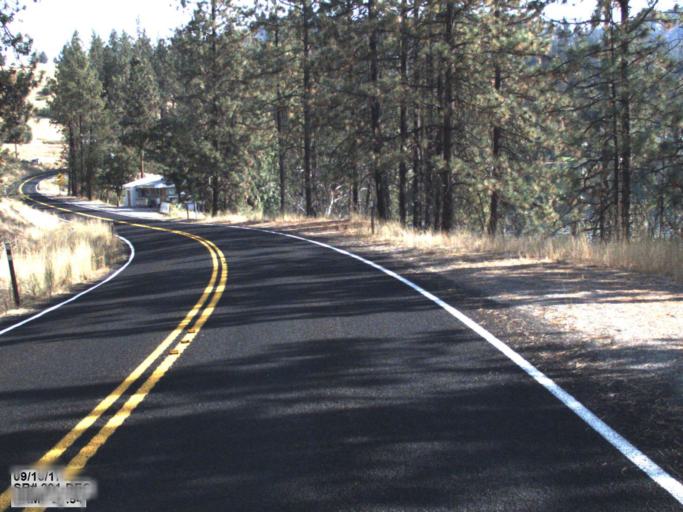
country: US
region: Washington
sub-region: Spokane County
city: Deer Park
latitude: 47.8922
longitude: -117.6707
